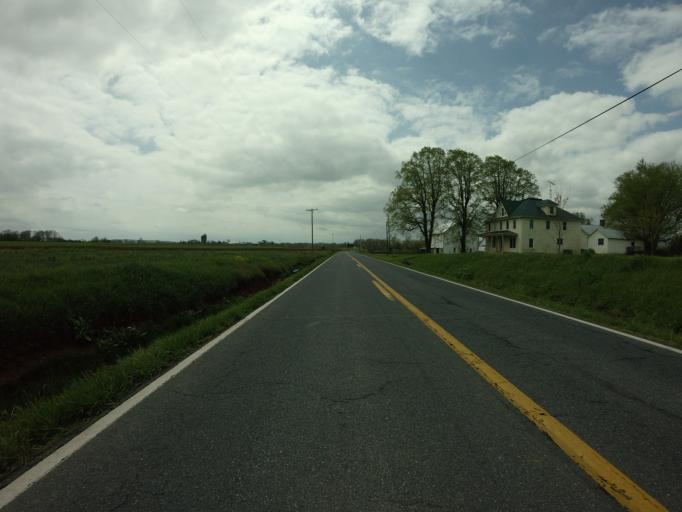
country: US
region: Maryland
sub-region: Frederick County
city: Thurmont
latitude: 39.5948
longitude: -77.3583
